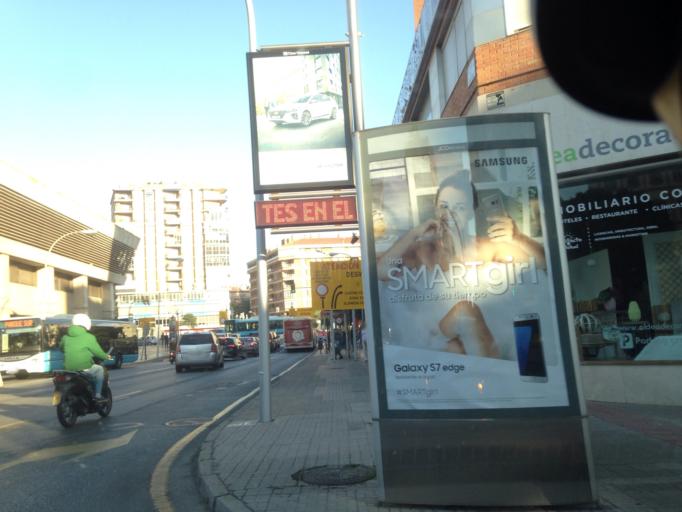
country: ES
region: Andalusia
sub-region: Provincia de Malaga
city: Malaga
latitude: 36.7157
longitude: -4.4275
